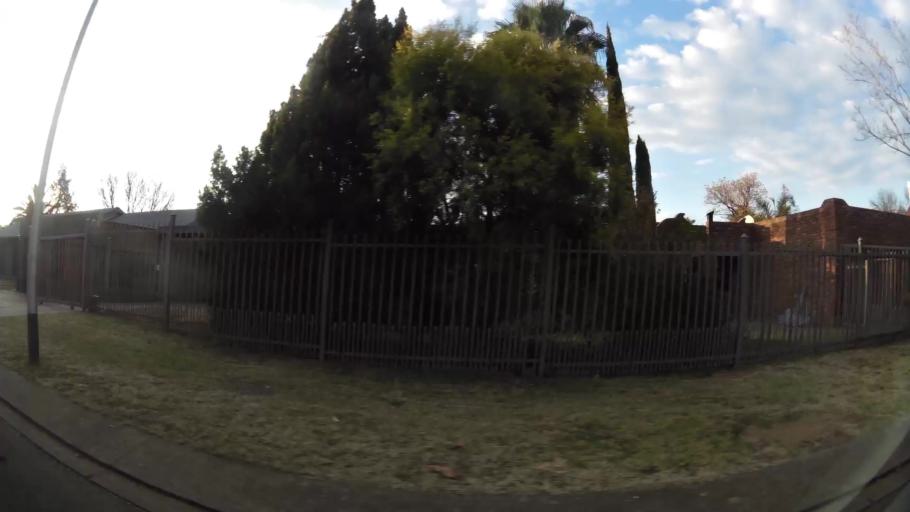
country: ZA
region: Orange Free State
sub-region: Mangaung Metropolitan Municipality
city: Bloemfontein
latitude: -29.1385
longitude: 26.1823
